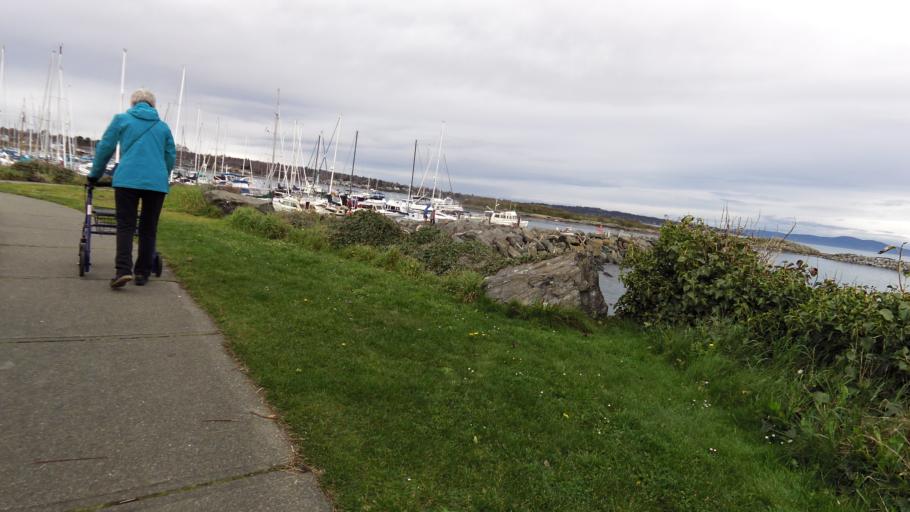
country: CA
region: British Columbia
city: Oak Bay
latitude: 48.4249
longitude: -123.3005
